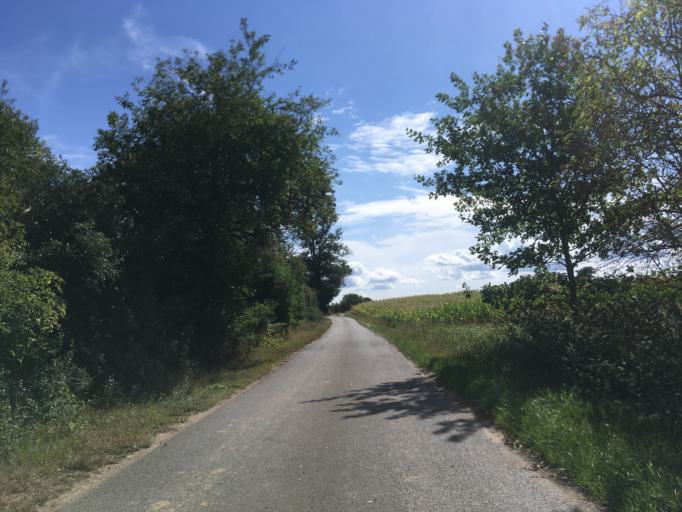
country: DE
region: Brandenburg
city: Gerswalde
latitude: 53.1588
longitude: 13.7594
